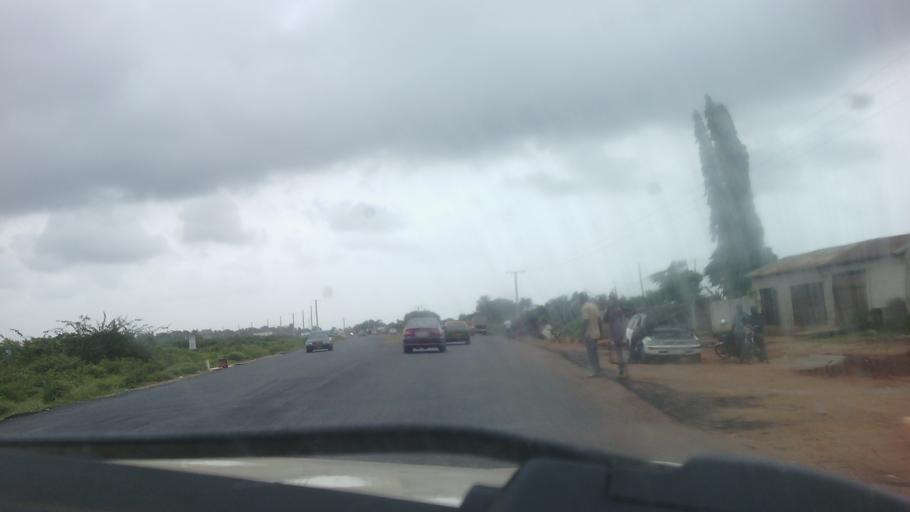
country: BJ
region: Atlantique
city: Ouidah
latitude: 6.3653
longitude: 2.0492
